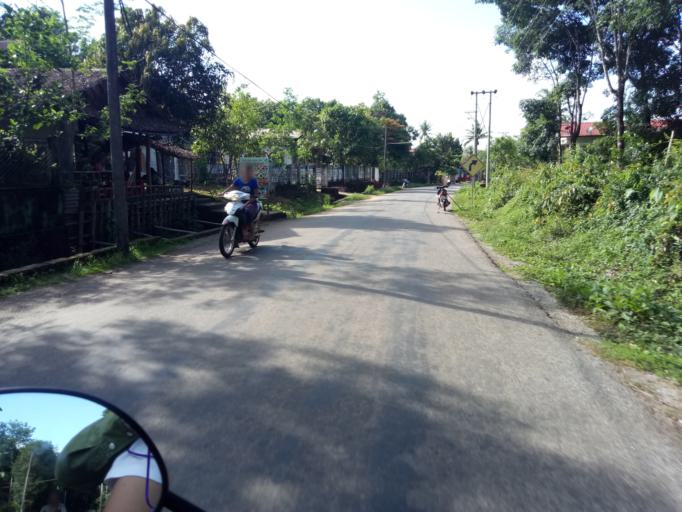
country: MM
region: Mon
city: Mawlamyine
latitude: 16.3840
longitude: 97.5491
